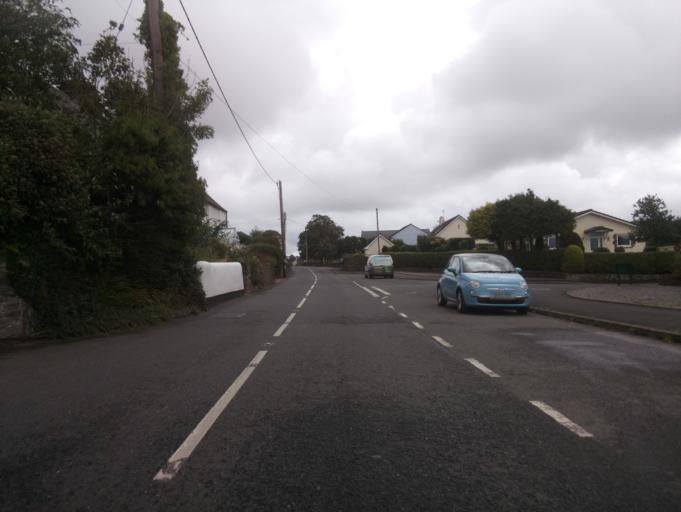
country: GB
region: England
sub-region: Devon
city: Kingsbridge
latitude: 50.2728
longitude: -3.7012
